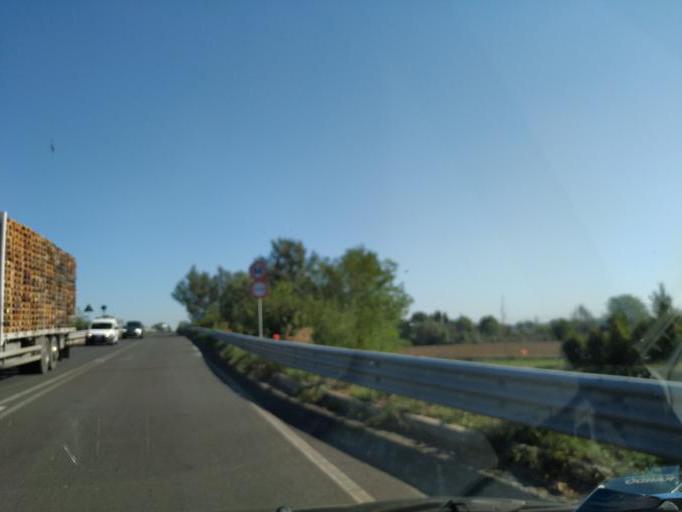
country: IT
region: Emilia-Romagna
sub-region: Provincia di Bologna
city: San Giovanni in Persiceto
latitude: 44.6537
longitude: 11.1789
